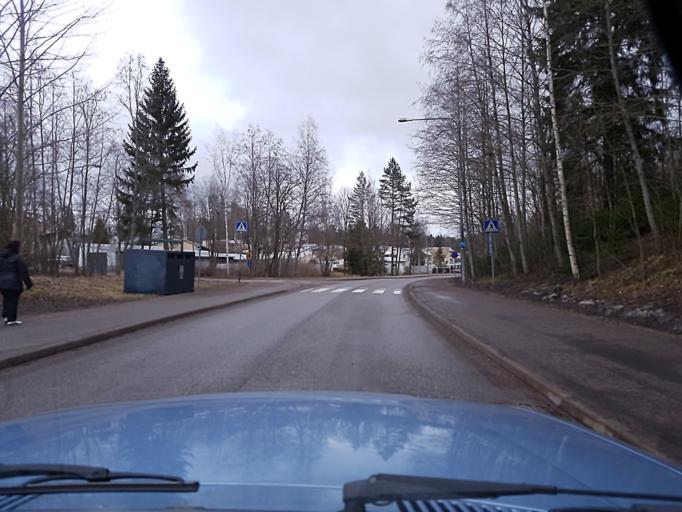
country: FI
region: Uusimaa
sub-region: Helsinki
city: Kauniainen
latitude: 60.2036
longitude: 24.7295
